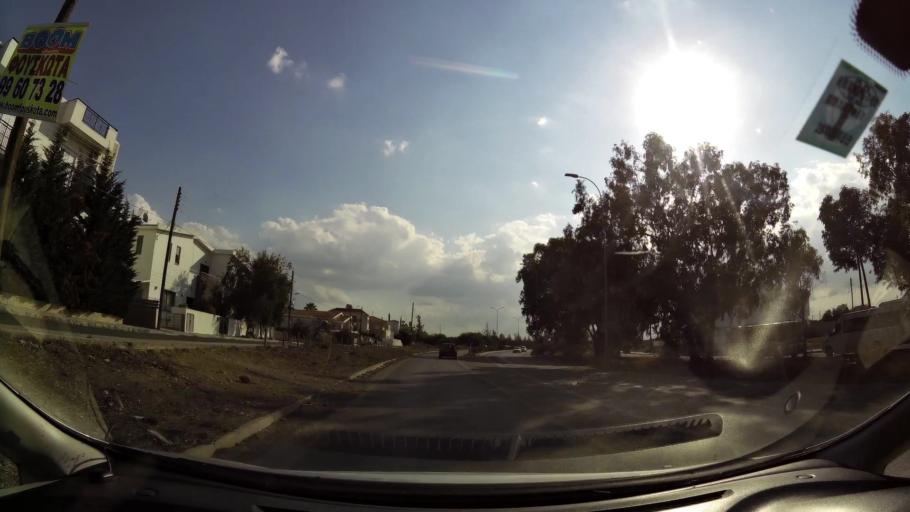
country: CY
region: Lefkosia
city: Kato Deftera
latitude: 35.1333
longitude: 33.3000
